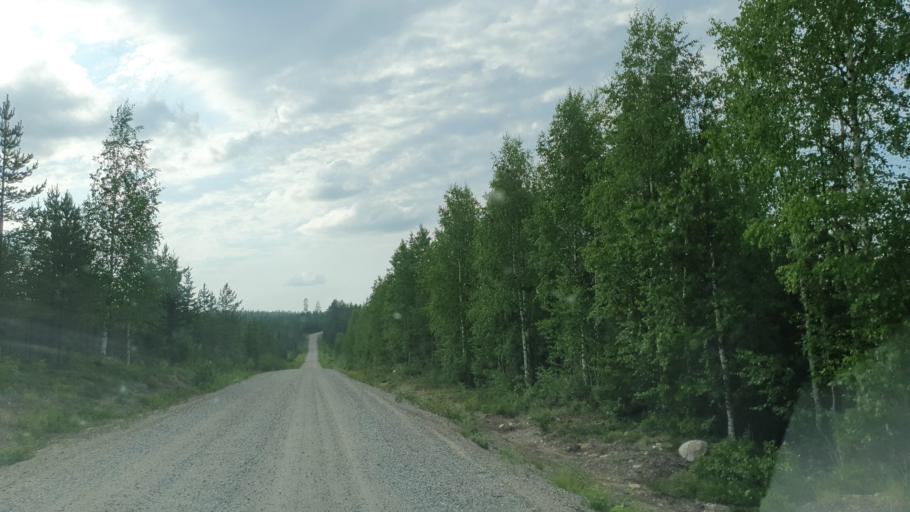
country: FI
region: Kainuu
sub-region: Kehys-Kainuu
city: Kuhmo
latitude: 64.0228
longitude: 29.8791
